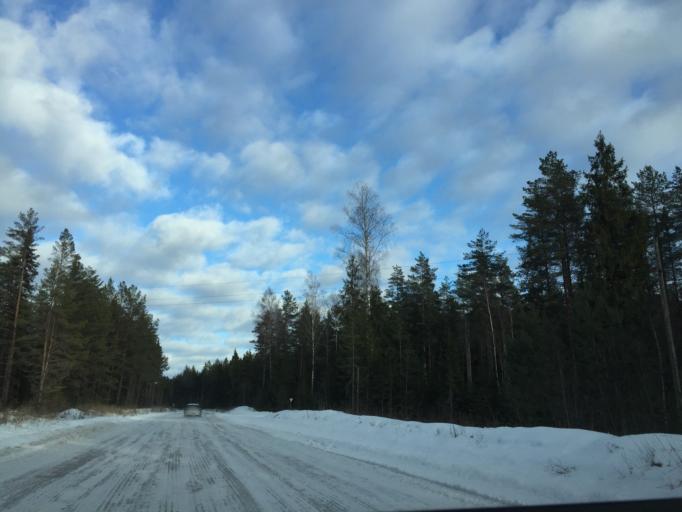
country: LV
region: Ogre
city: Jumprava
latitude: 56.5699
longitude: 24.9336
